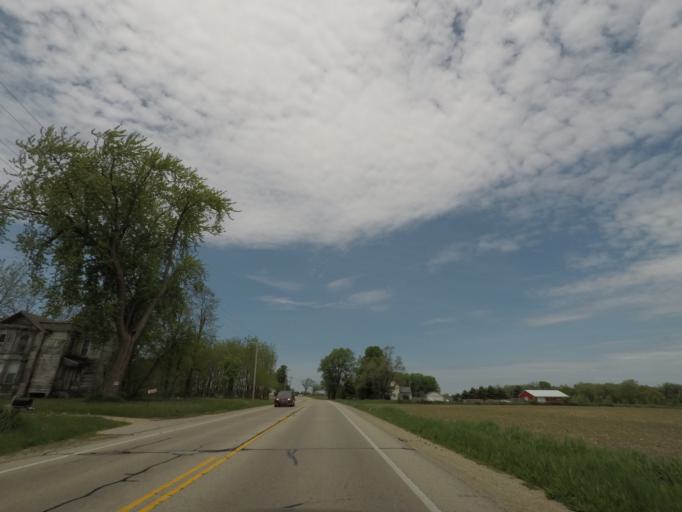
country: US
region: Wisconsin
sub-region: Green County
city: Brooklyn
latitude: 42.8441
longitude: -89.3280
